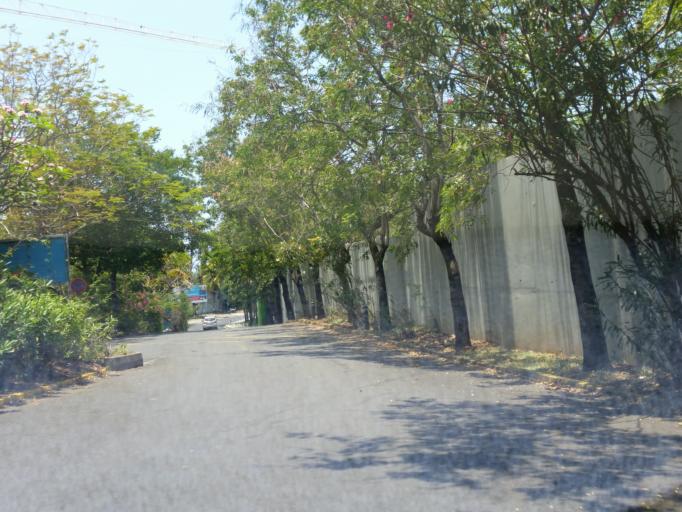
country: RE
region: Reunion
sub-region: Reunion
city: Saint-Denis
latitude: -20.8950
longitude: 55.4741
